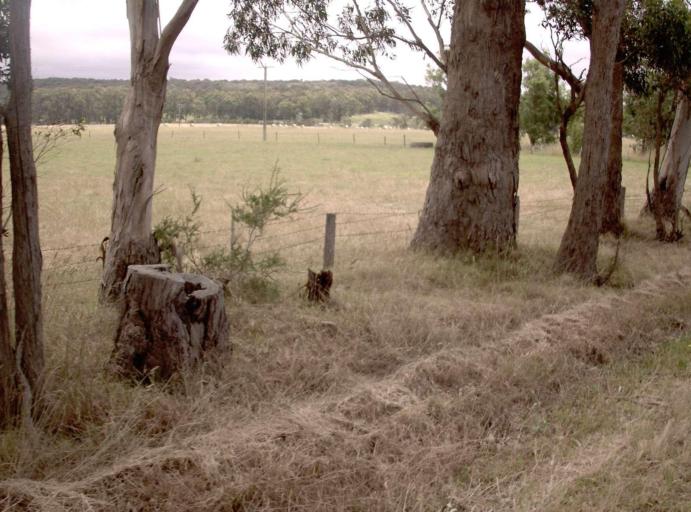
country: AU
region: Victoria
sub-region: Latrobe
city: Traralgon
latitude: -38.5133
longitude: 146.6488
